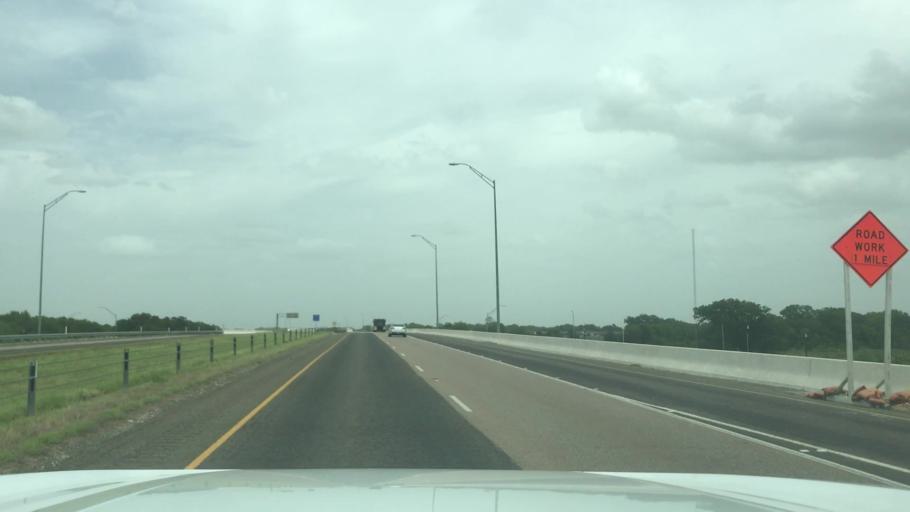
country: US
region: Texas
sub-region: McLennan County
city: Beverly
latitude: 31.5173
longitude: -97.0917
